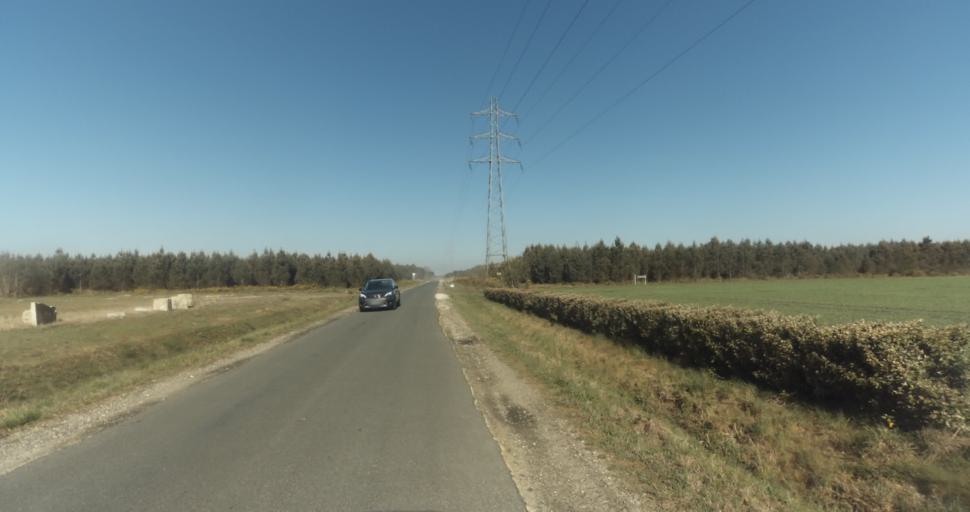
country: FR
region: Aquitaine
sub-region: Departement de la Gironde
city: Marcheprime
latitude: 44.7479
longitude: -0.8412
